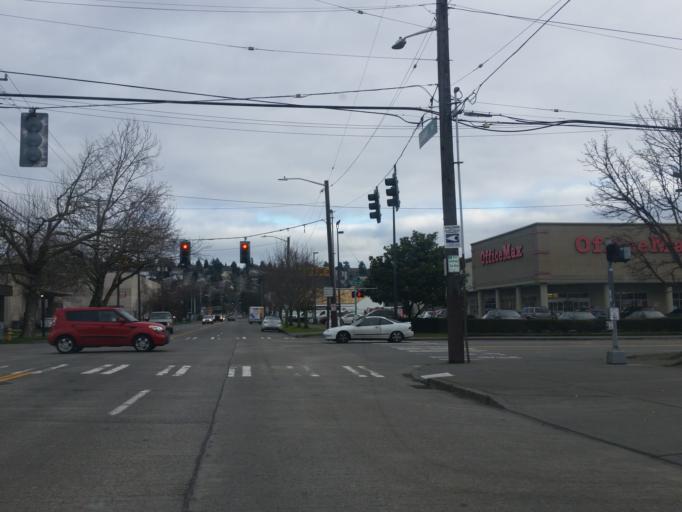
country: US
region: Washington
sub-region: King County
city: Seattle
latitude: 47.6636
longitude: -122.3741
